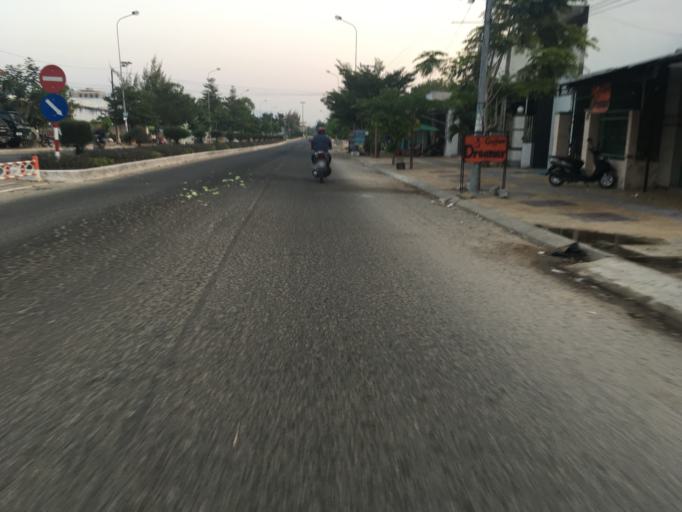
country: VN
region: Ninh Thuan
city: Phan Rang-Thap Cham
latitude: 11.5600
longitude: 109.0213
